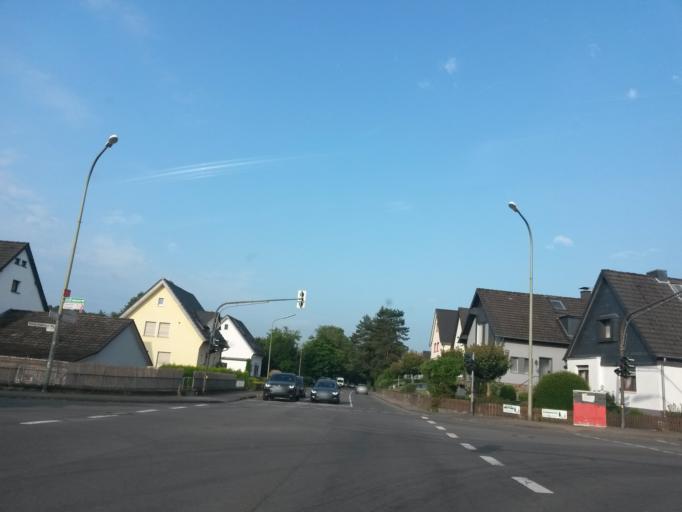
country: DE
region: North Rhine-Westphalia
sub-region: Regierungsbezirk Koln
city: Lindlar
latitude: 51.0173
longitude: 7.3703
